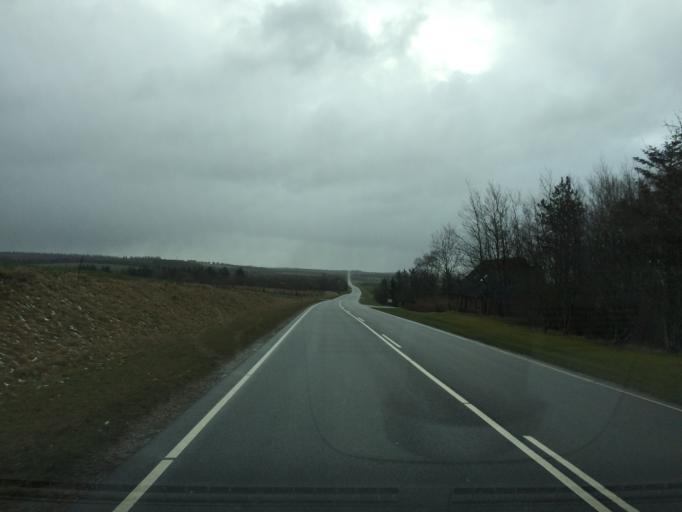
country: DK
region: Central Jutland
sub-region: Ringkobing-Skjern Kommune
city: Videbaek
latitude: 56.1921
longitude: 8.5781
